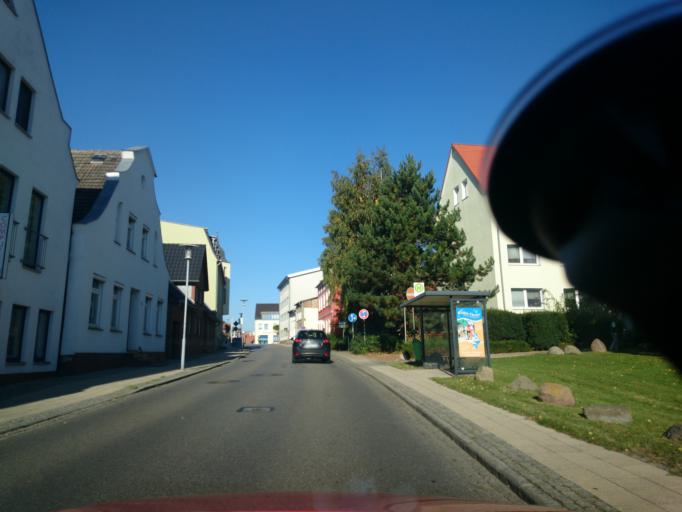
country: DE
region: Mecklenburg-Vorpommern
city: Ribnitz-Damgarten
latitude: 54.2509
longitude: 12.4728
